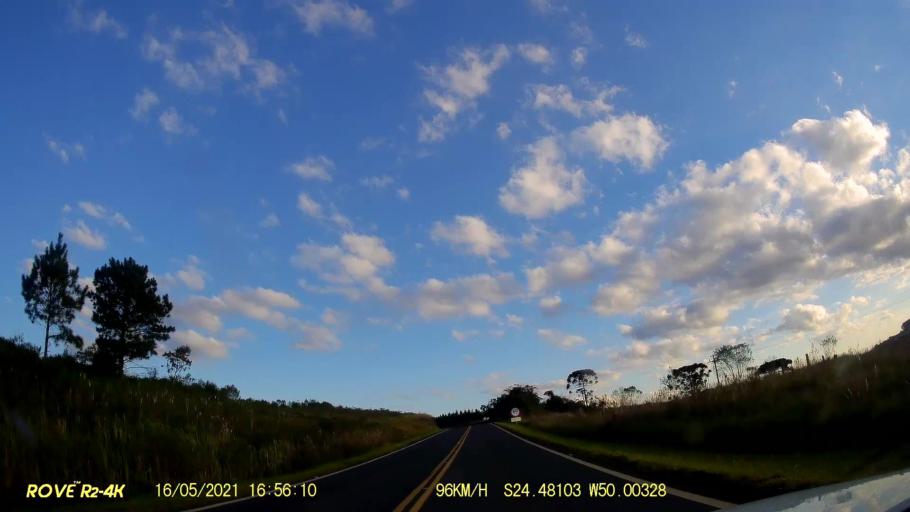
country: BR
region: Parana
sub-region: Pirai Do Sul
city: Pirai do Sul
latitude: -24.4810
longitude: -50.0033
